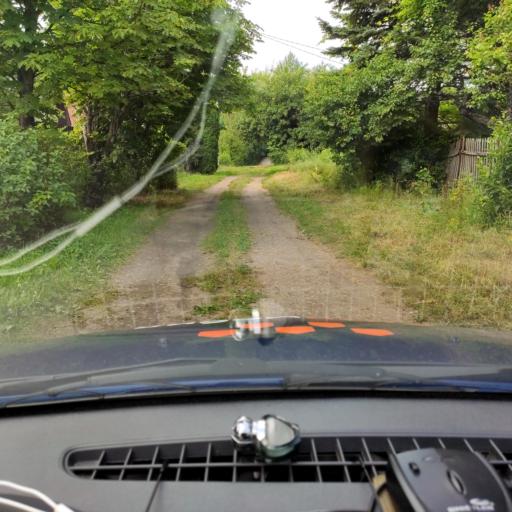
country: RU
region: Voronezj
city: Ramon'
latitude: 52.0751
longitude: 39.3092
